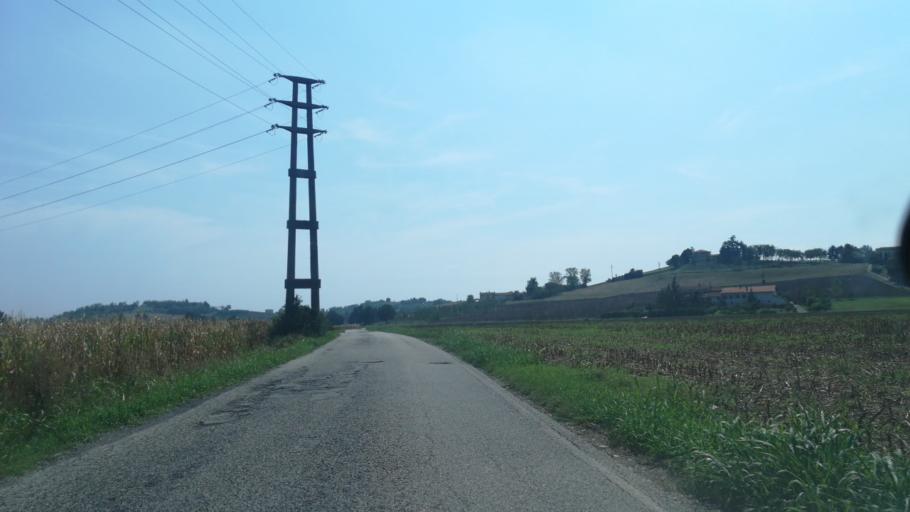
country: IT
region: Piedmont
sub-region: Provincia di Alessandria
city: San Giorgio Monferrato
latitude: 45.1076
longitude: 8.4415
